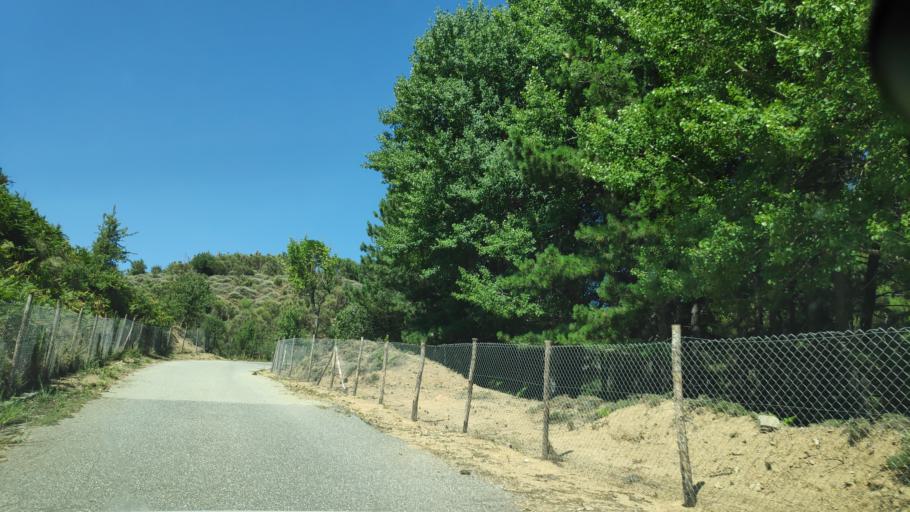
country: IT
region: Calabria
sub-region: Provincia di Reggio Calabria
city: Bova
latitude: 38.0196
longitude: 15.9346
